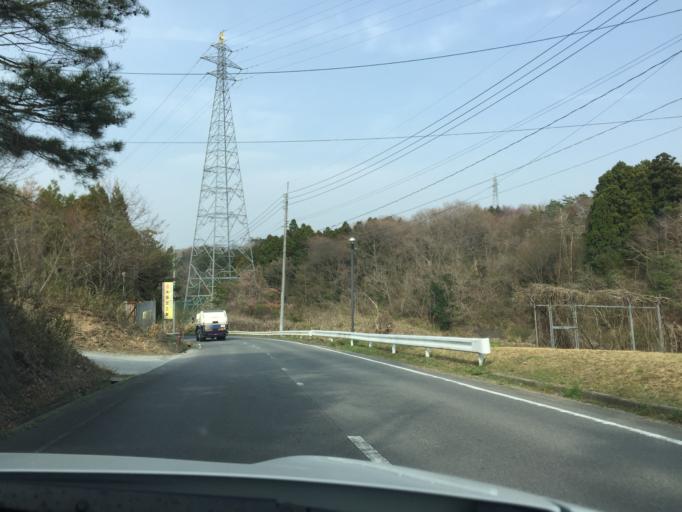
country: JP
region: Fukushima
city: Iwaki
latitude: 36.9703
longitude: 140.8538
